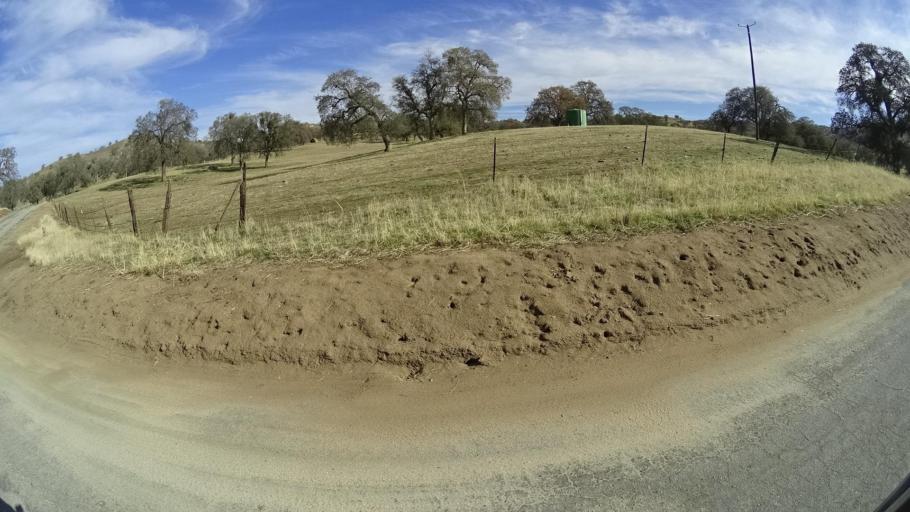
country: US
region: California
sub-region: Kern County
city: Oildale
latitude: 35.5824
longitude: -118.8231
